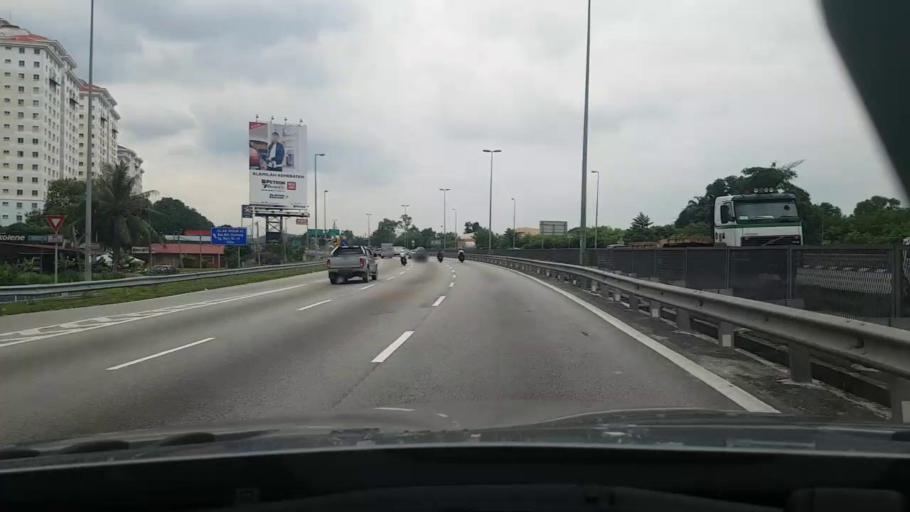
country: MY
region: Selangor
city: Subang Jaya
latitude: 2.9881
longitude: 101.6230
